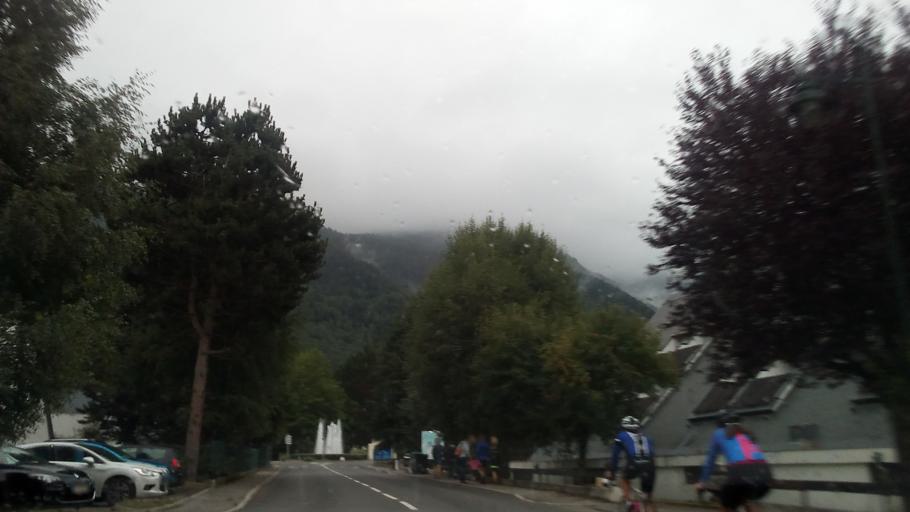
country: FR
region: Midi-Pyrenees
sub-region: Departement des Hautes-Pyrenees
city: Saint-Lary-Soulan
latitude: 42.8209
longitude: 0.3226
